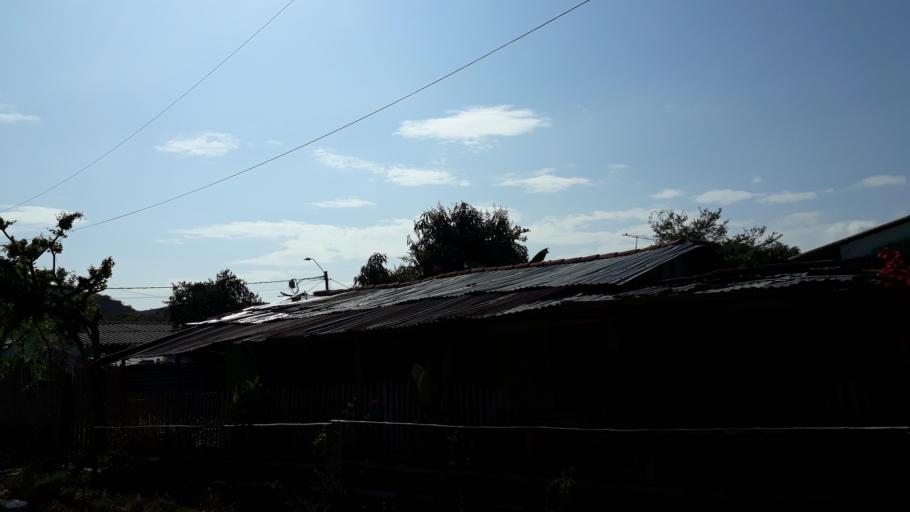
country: CO
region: Cauca
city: Buenos Aires
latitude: 3.1256
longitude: -76.6229
